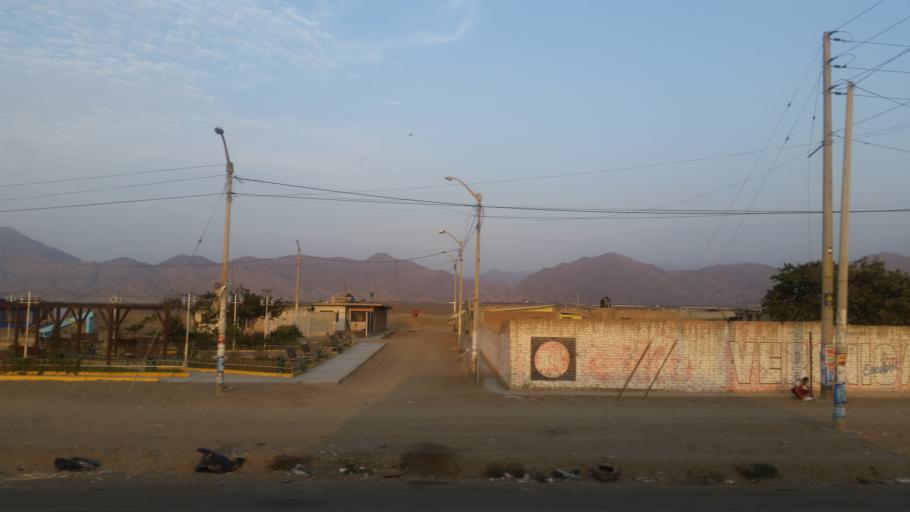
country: PE
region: La Libertad
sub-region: Ascope
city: Chicama
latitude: -7.8721
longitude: -79.1340
